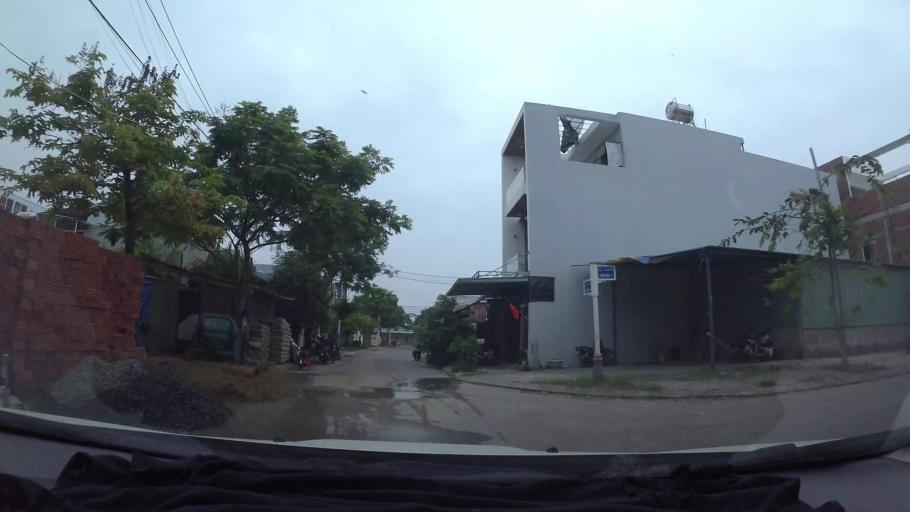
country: VN
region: Da Nang
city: Thanh Khe
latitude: 16.0444
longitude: 108.1768
